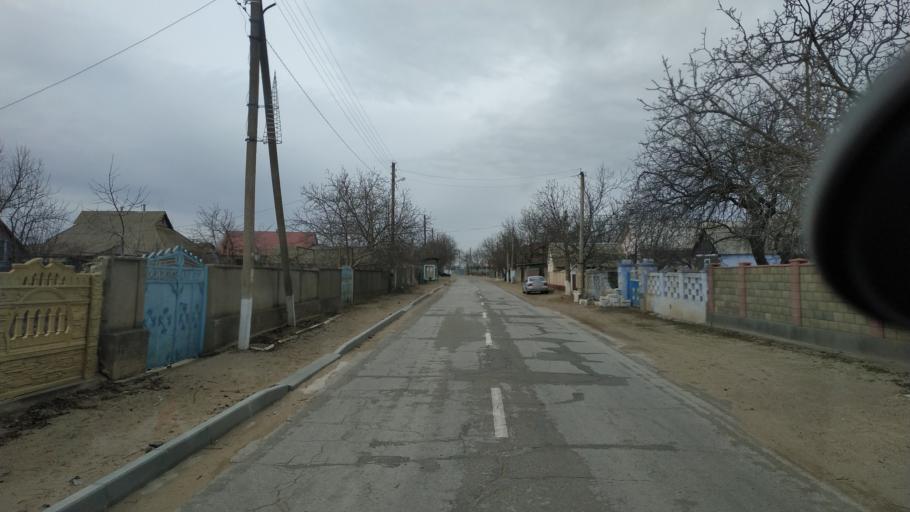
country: MD
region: Telenesti
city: Cocieri
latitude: 47.3155
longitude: 29.1044
